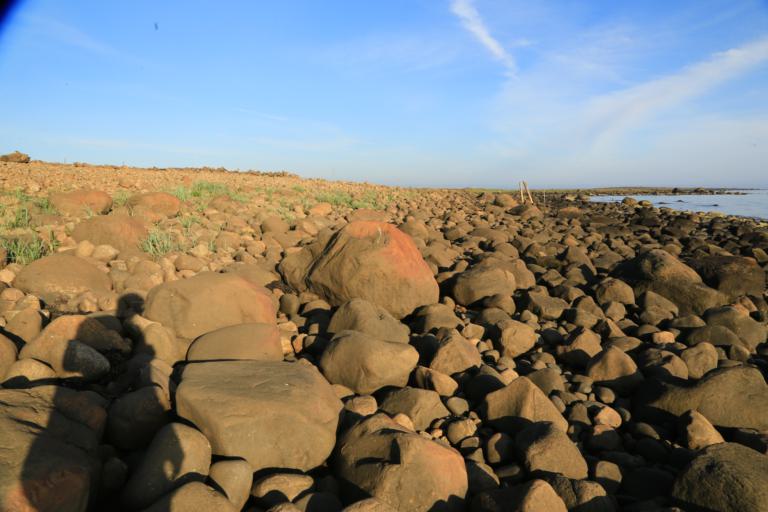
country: SE
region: Halland
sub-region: Varbergs Kommun
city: Traslovslage
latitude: 57.0362
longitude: 12.2966
